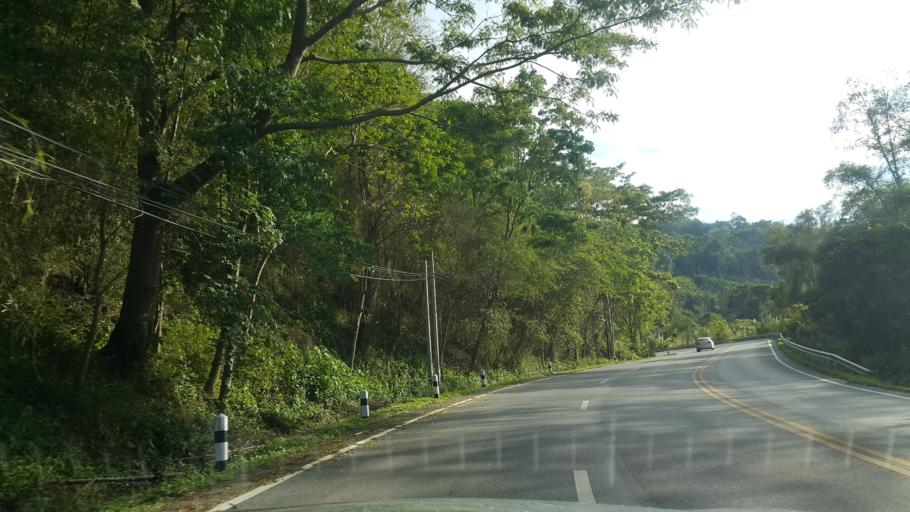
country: TH
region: Phayao
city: Phayao
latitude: 19.0618
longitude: 99.8015
